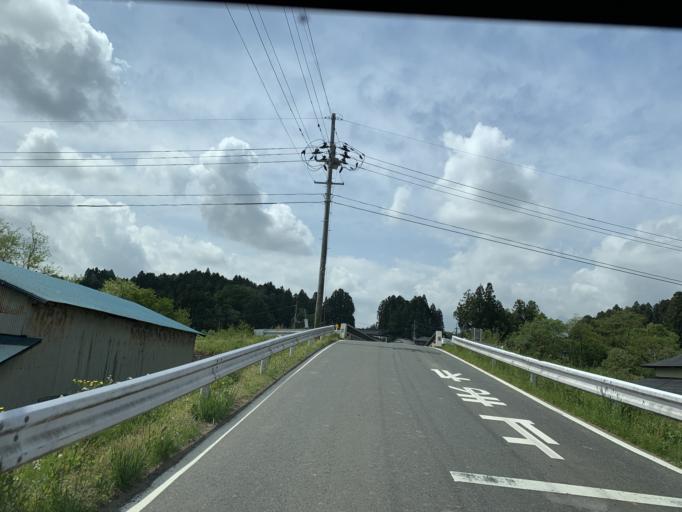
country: JP
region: Iwate
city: Ichinoseki
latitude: 38.7917
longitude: 141.0035
